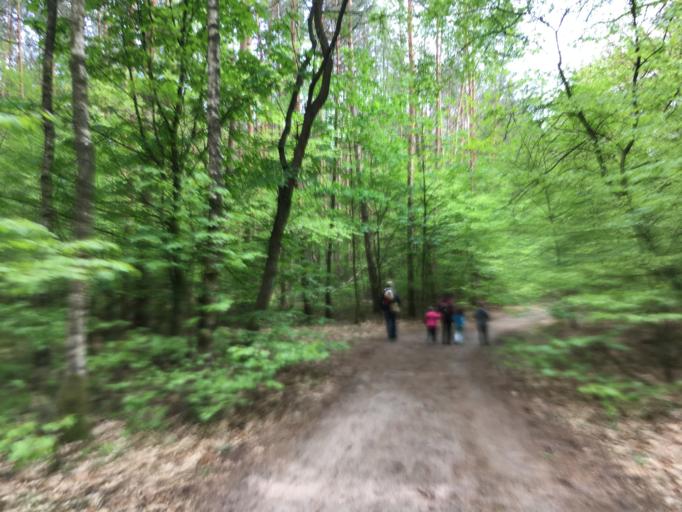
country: DE
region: Brandenburg
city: Rudnitz
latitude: 52.7343
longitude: 13.5972
